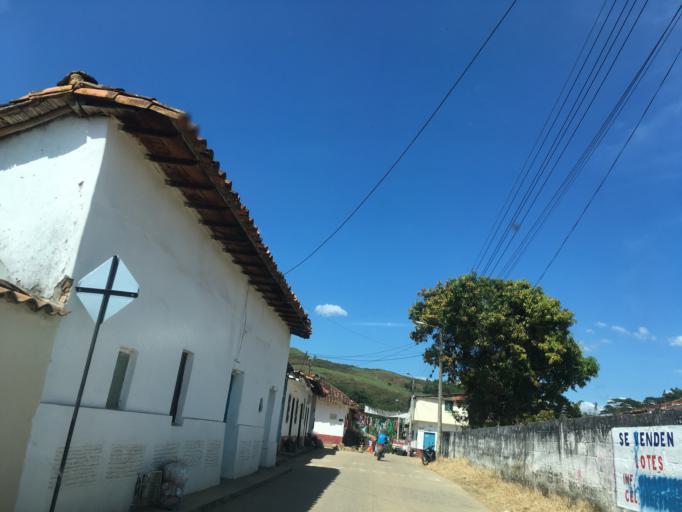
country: CO
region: Santander
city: Coromoro
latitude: 6.2864
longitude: -73.1506
